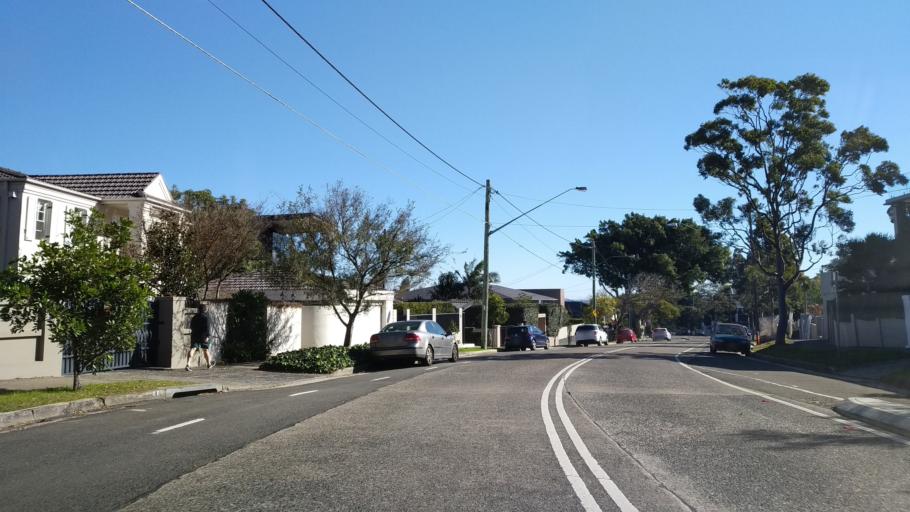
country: AU
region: New South Wales
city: Edgecliff
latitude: -33.8846
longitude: 151.2547
